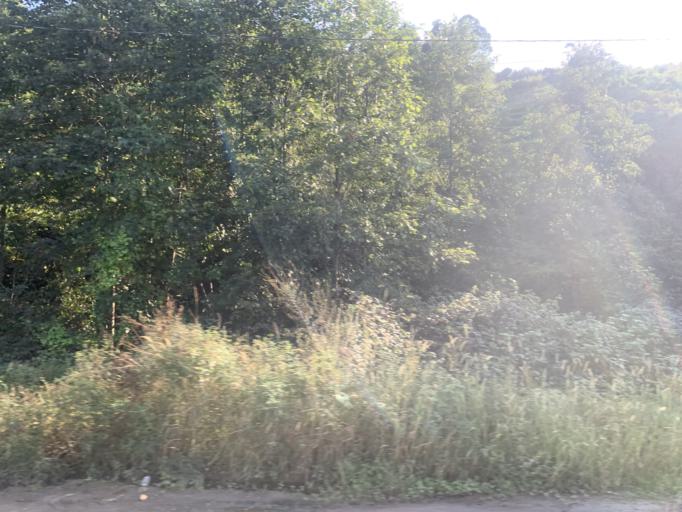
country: TR
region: Trabzon
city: Of
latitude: 40.9261
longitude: 40.2242
